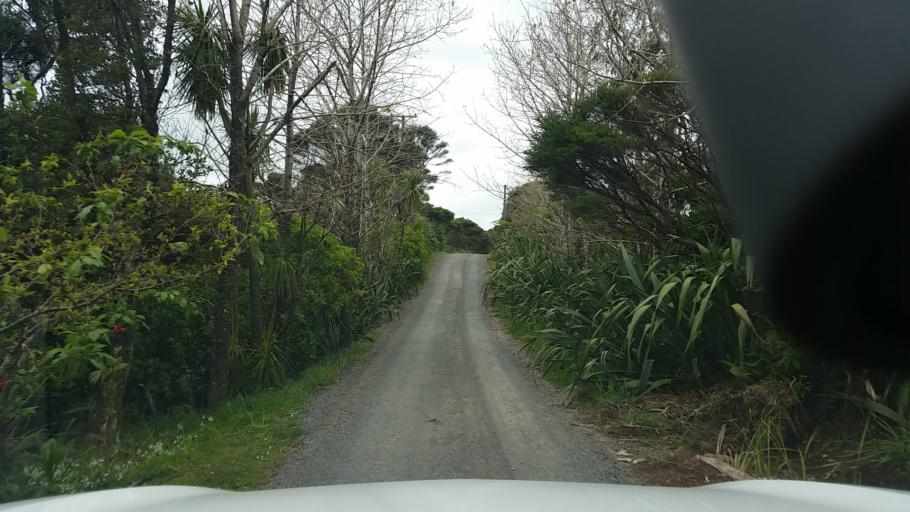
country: NZ
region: Auckland
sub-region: Auckland
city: Muriwai Beach
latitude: -36.8770
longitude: 174.4644
